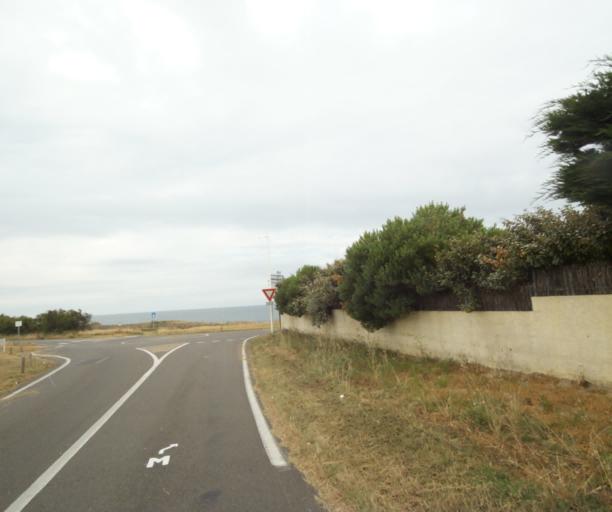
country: FR
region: Pays de la Loire
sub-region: Departement de la Vendee
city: Chateau-d'Olonne
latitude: 46.4655
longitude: -1.7317
